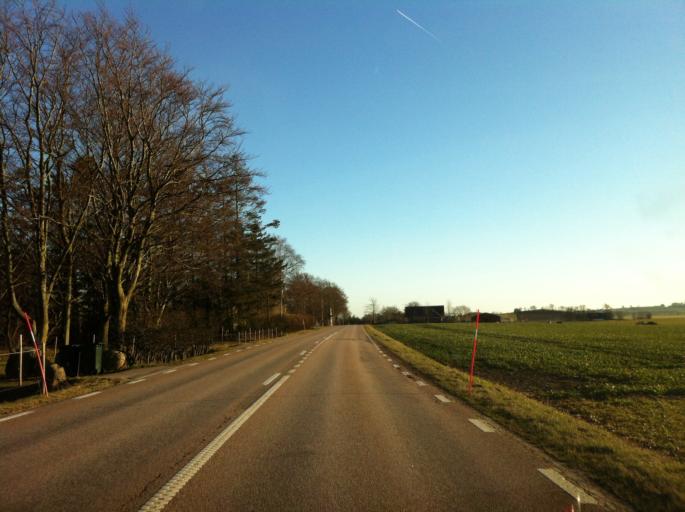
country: SE
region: Skane
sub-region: Landskrona
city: Asmundtorp
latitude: 55.9615
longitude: 12.9446
